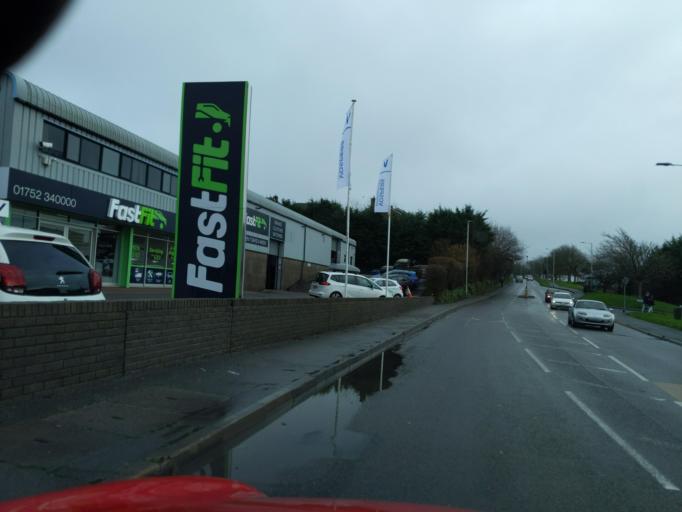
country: GB
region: England
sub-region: Devon
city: Plympton
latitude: 50.3826
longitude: -4.0312
